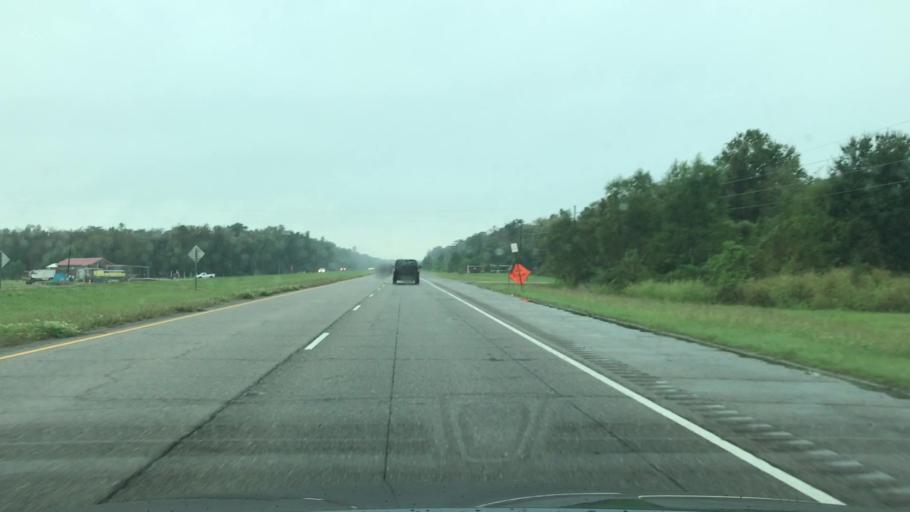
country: US
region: Louisiana
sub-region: Lafourche Parish
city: Raceland
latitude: 29.7381
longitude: -90.5576
